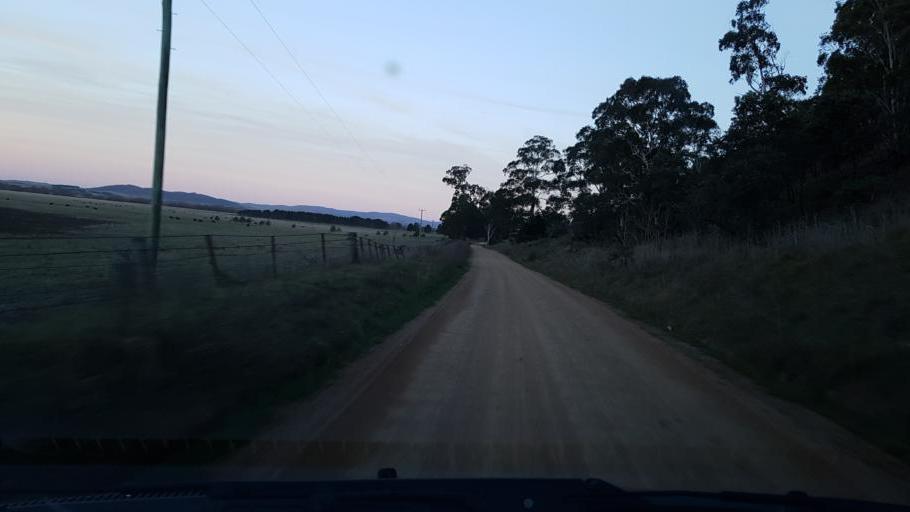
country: AU
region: New South Wales
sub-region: Palerang
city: Bungendore
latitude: -35.2021
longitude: 149.4010
